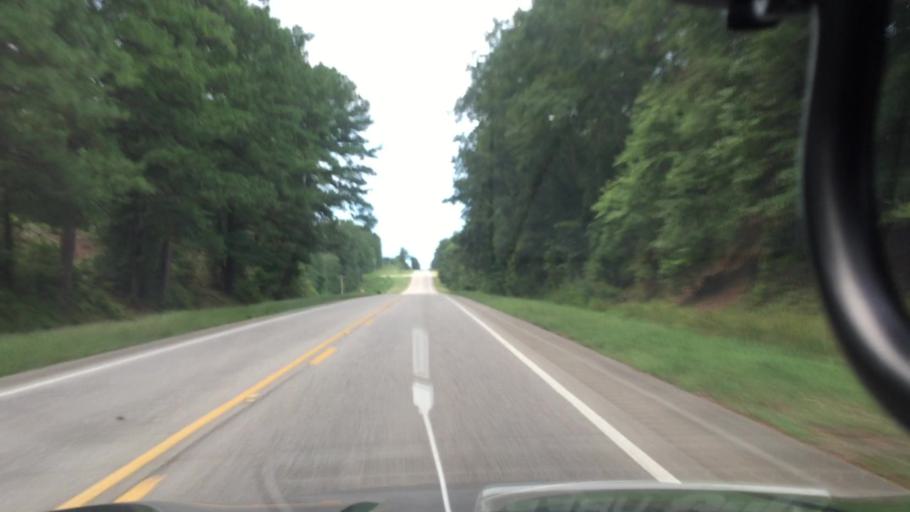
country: US
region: Alabama
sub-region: Pike County
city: Brundidge
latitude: 31.6597
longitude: -85.9524
